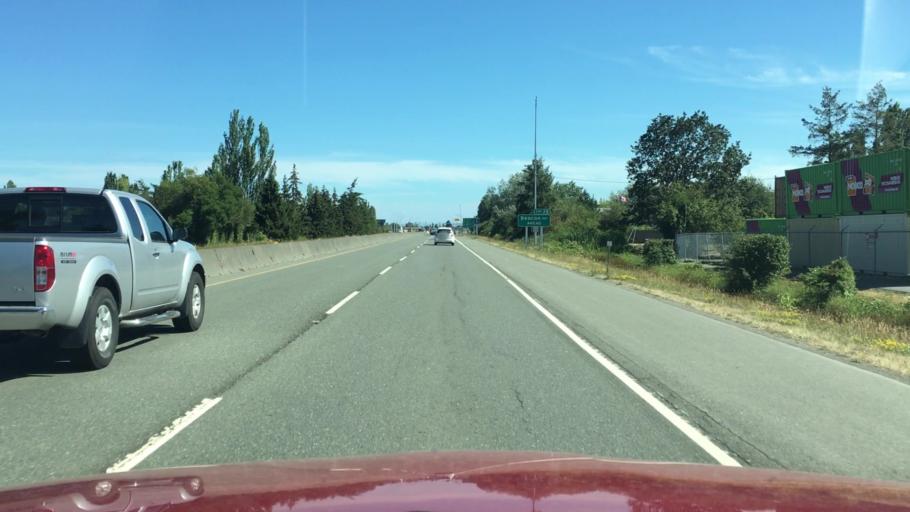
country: CA
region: British Columbia
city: North Saanich
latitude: 48.6538
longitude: -123.4107
